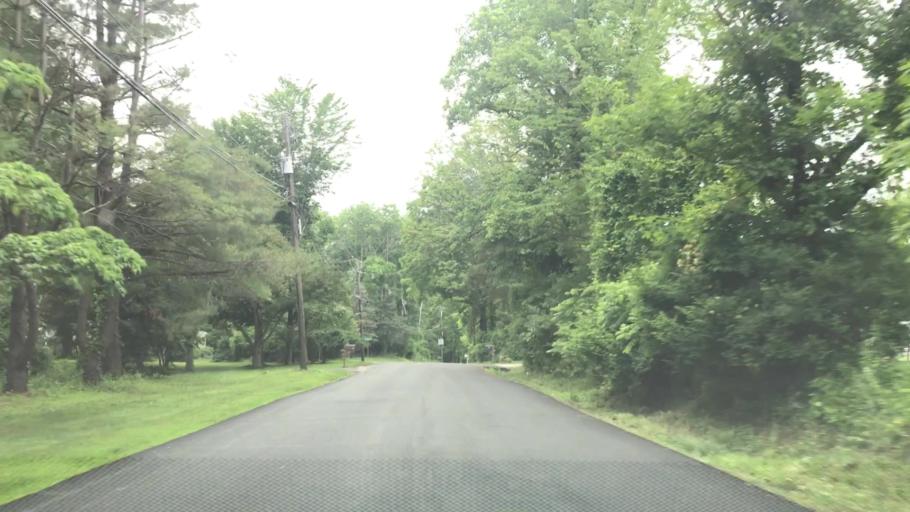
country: US
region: New Jersey
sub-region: Hunterdon County
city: Lebanon
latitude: 40.6591
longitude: -74.8307
